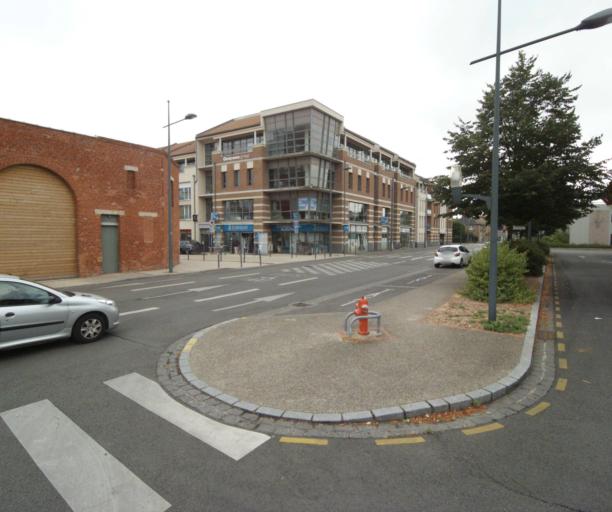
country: FR
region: Nord-Pas-de-Calais
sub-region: Departement du Nord
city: Armentieres
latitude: 50.6810
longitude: 2.8781
